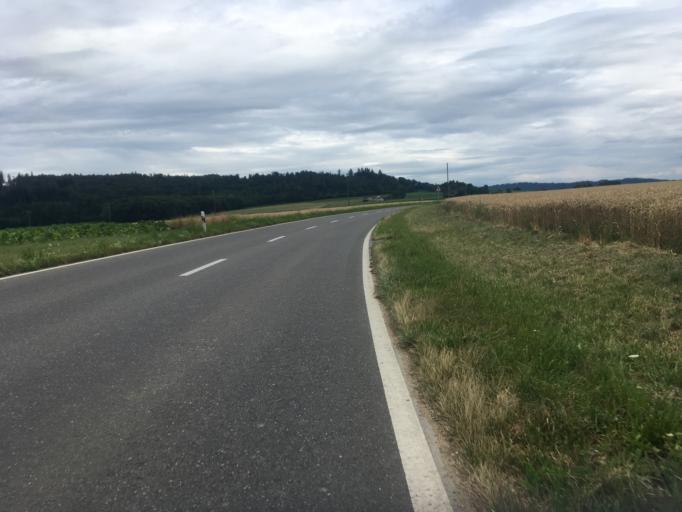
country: CH
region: Bern
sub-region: Seeland District
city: Erlach
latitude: 47.0292
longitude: 7.0958
